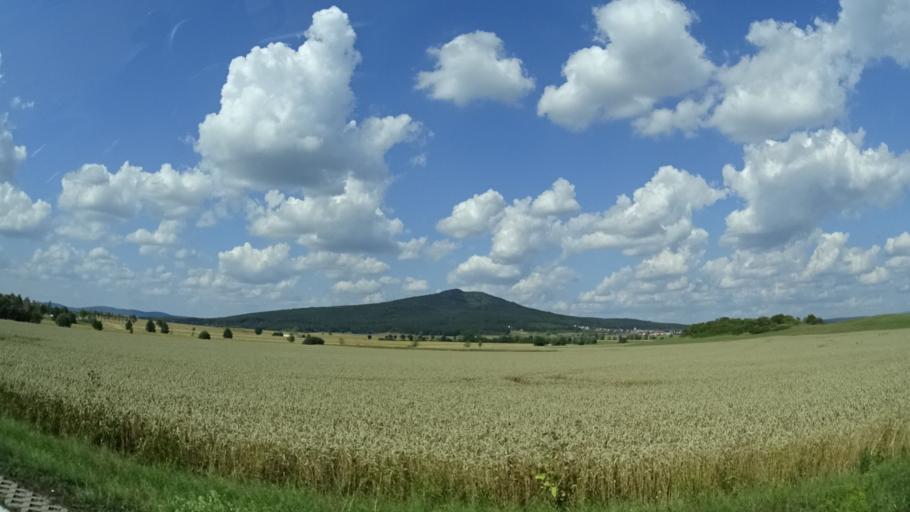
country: DE
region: Bavaria
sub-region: Regierungsbezirk Unterfranken
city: Trappstadt
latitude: 50.3469
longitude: 10.5773
